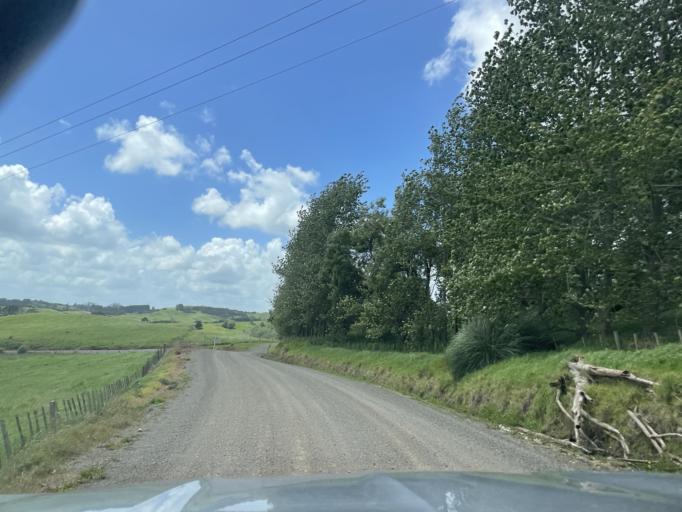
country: NZ
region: Auckland
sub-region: Auckland
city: Wellsford
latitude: -36.1667
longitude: 174.3207
